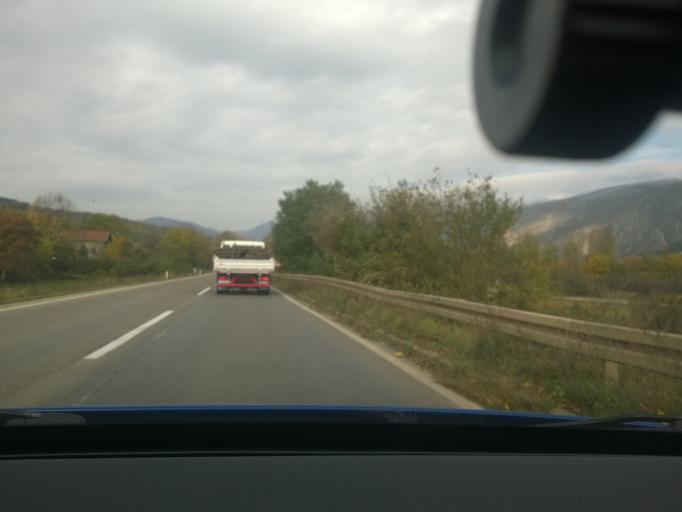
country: RS
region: Central Serbia
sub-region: Pirotski Okrug
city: Bela Palanka
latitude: 43.2771
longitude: 22.2274
